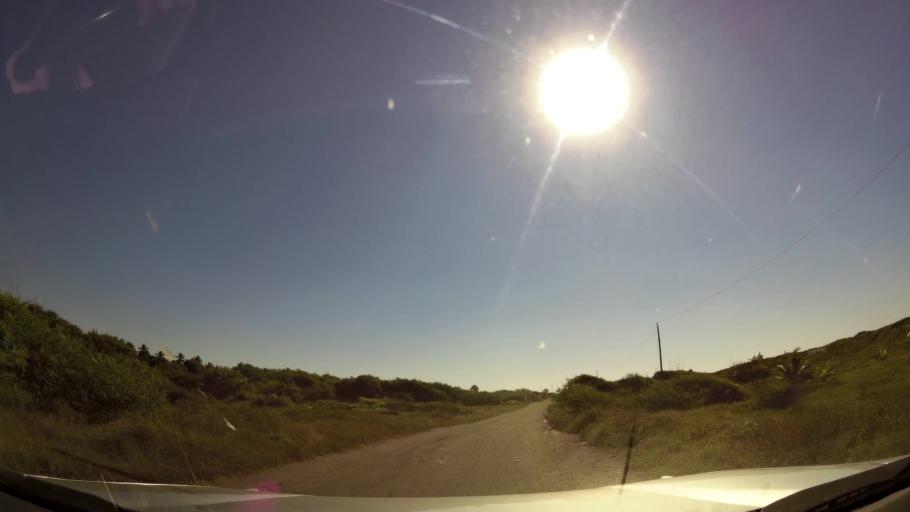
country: GT
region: Jutiapa
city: Pasaco
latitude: 13.8494
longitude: -90.3727
